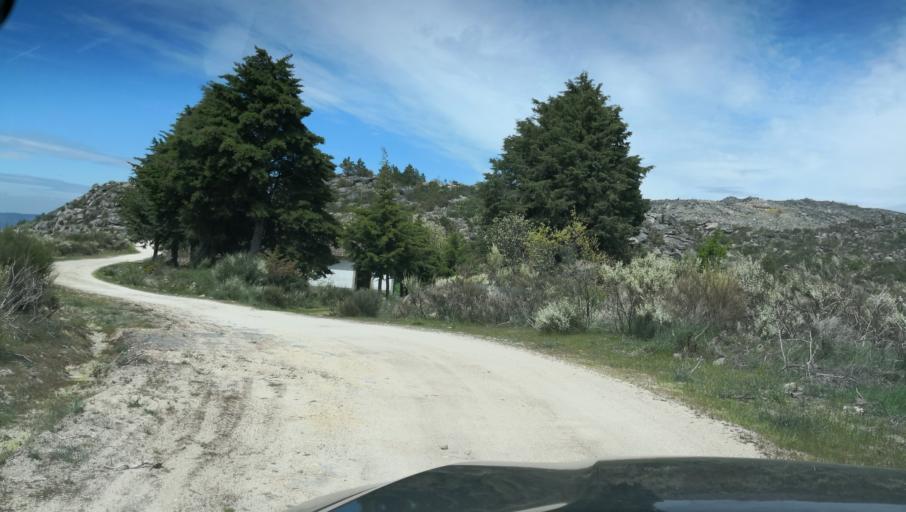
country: PT
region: Vila Real
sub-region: Vila Real
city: Vila Real
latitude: 41.3793
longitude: -7.6712
